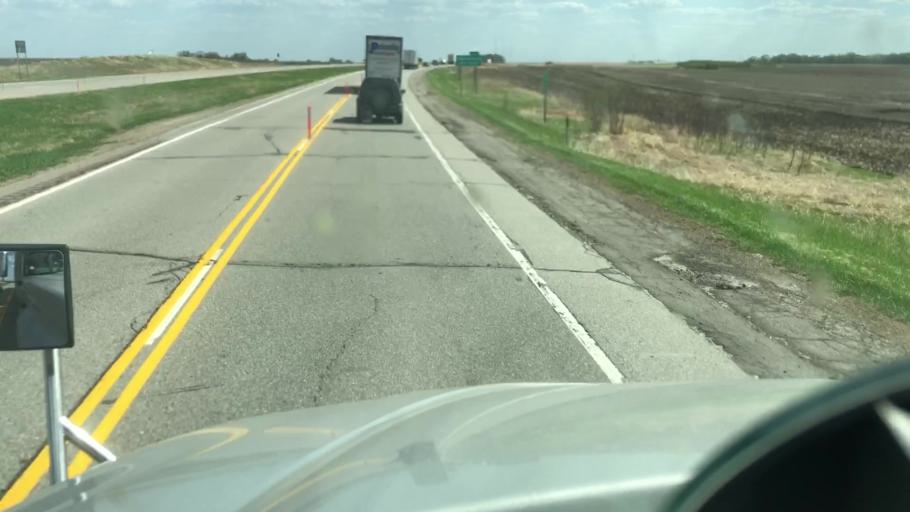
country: US
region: Minnesota
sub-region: Scott County
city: Belle Plaine
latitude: 44.5527
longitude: -93.8501
